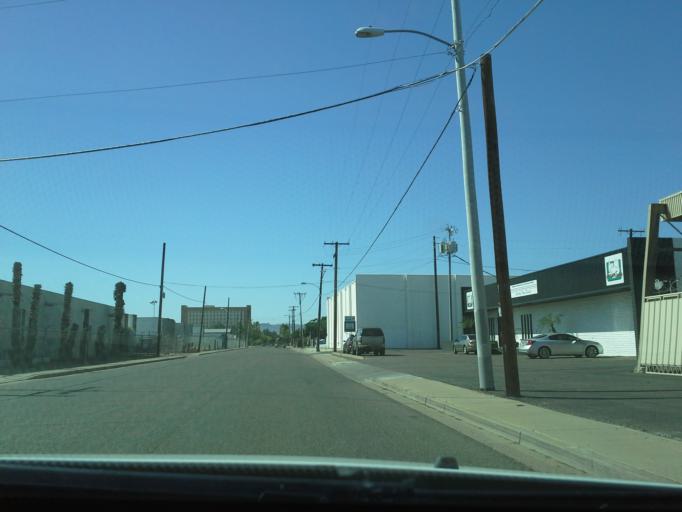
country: US
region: Arizona
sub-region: Maricopa County
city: Phoenix
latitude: 33.4575
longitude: -112.0957
